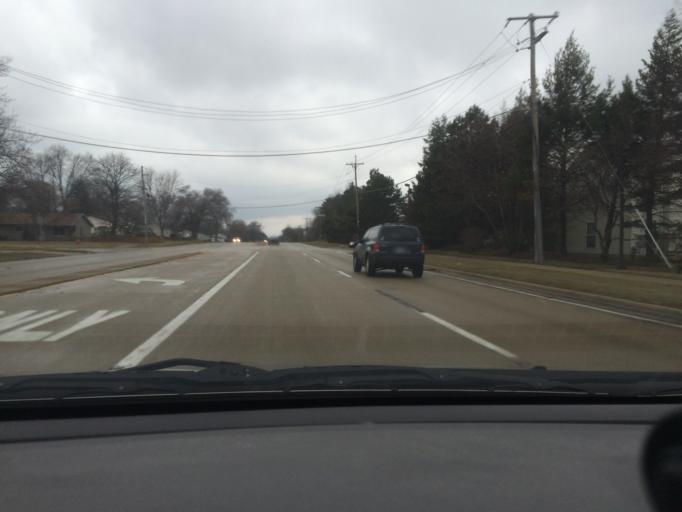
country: US
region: Illinois
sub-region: Cook County
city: Streamwood
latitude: 42.0318
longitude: -88.1731
